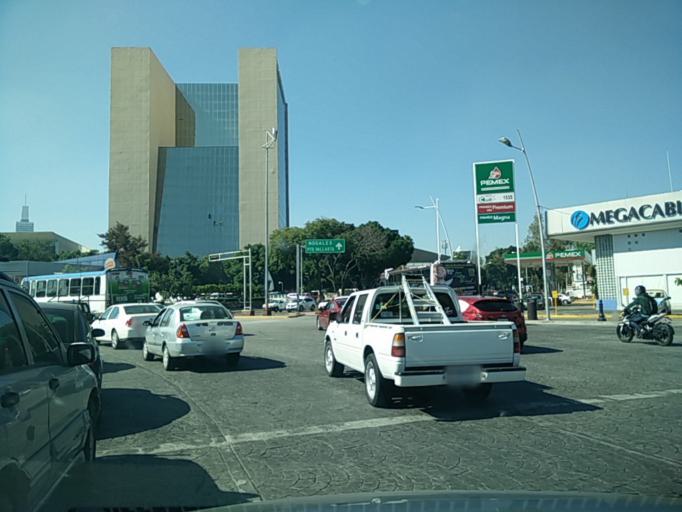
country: MX
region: Jalisco
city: Guadalajara
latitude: 20.6747
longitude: -103.3876
